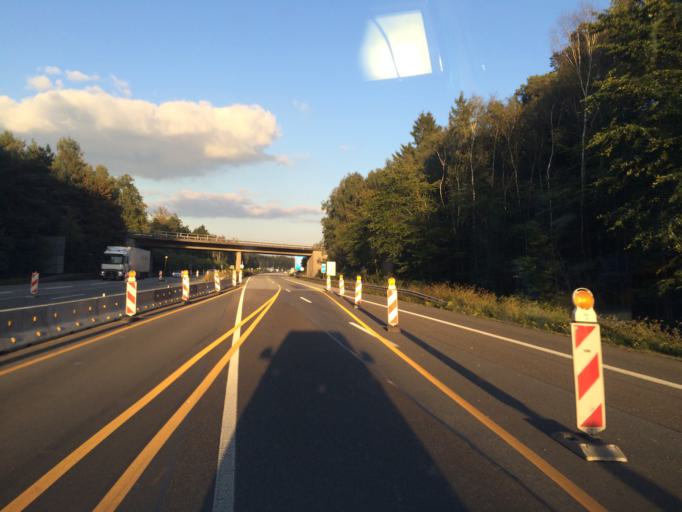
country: DE
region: Rheinland-Pfalz
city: Schonenberg-Kubelberg
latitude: 49.3707
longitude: 7.3633
